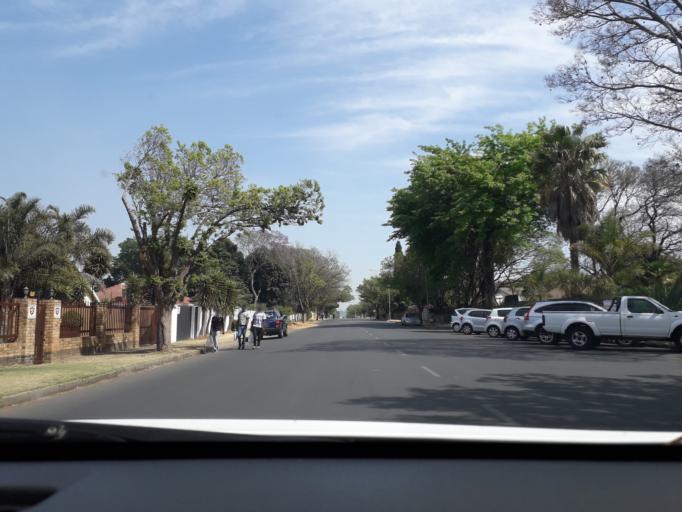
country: ZA
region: Gauteng
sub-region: City of Johannesburg Metropolitan Municipality
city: Modderfontein
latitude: -26.0962
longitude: 28.2381
